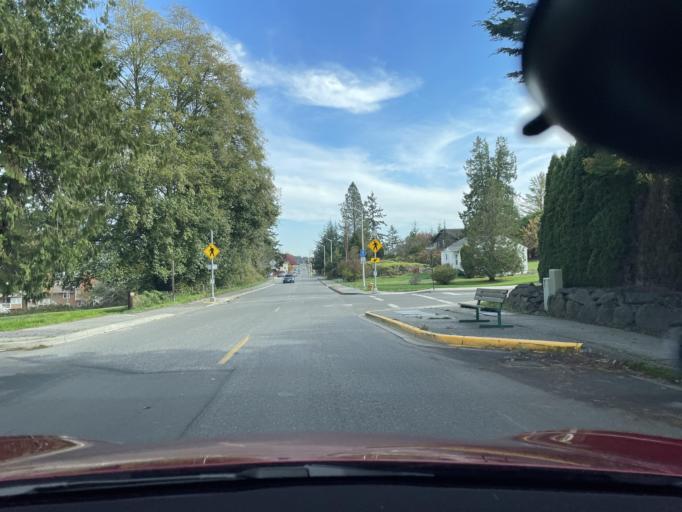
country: US
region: Washington
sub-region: San Juan County
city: Friday Harbor
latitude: 48.5362
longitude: -123.0273
